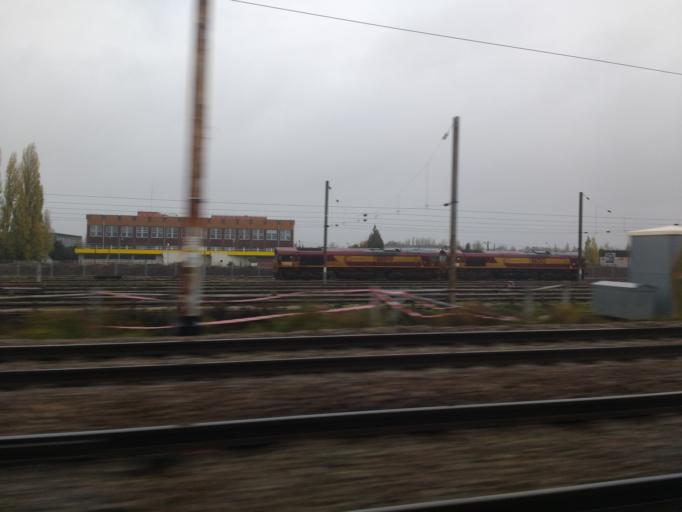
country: FR
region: Picardie
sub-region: Departement de la Somme
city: Rivery
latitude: 49.8890
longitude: 2.3208
